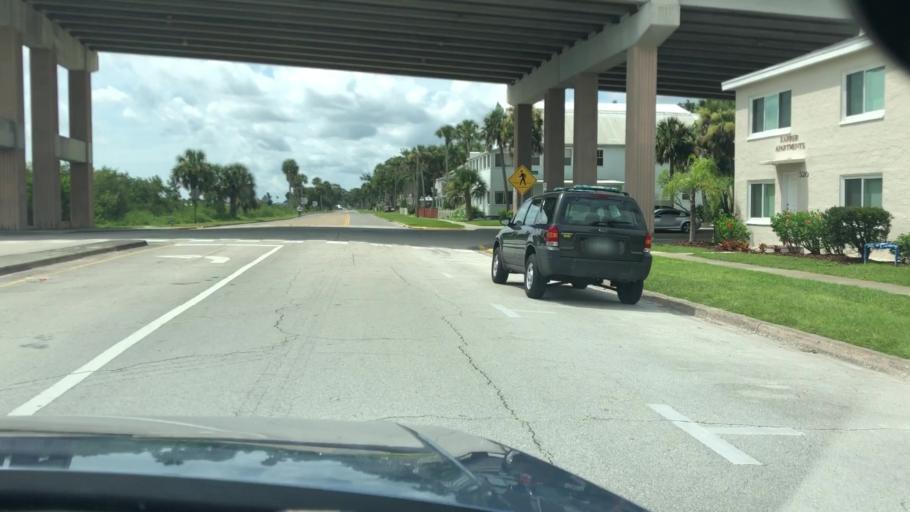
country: US
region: Florida
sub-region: Volusia County
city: New Smyrna Beach
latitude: 29.0233
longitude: -80.9201
